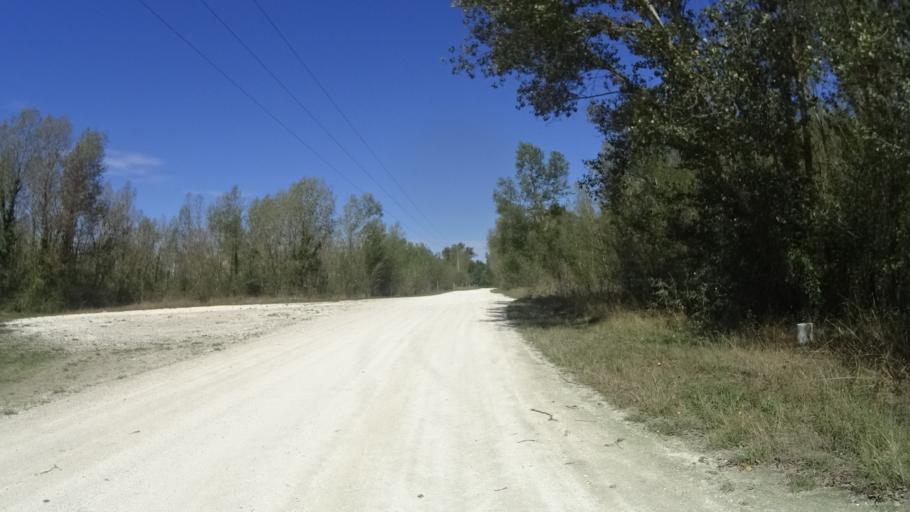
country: FR
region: Centre
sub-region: Departement du Loiret
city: Bonny-sur-Loire
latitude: 47.5441
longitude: 2.8360
